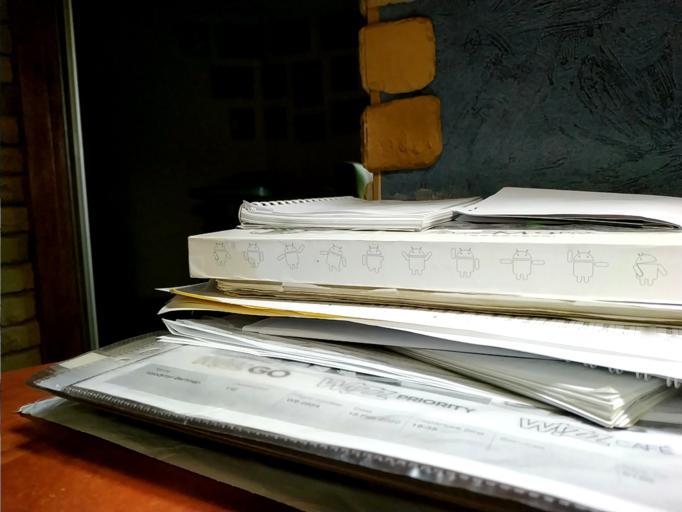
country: RU
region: Arkhangelskaya
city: Onega
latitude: 63.6719
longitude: 38.0445
